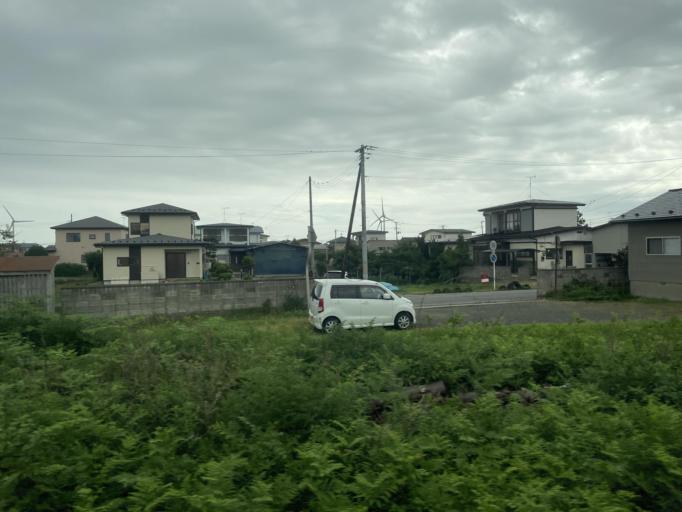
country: JP
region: Akita
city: Tenno
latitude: 39.8972
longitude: 139.9666
